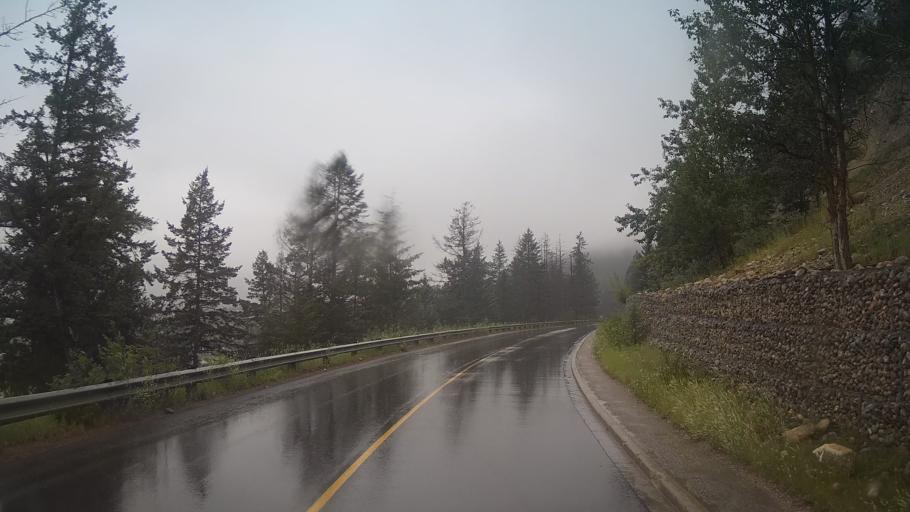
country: CA
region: Alberta
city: Jasper Park Lodge
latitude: 52.8881
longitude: -118.0813
